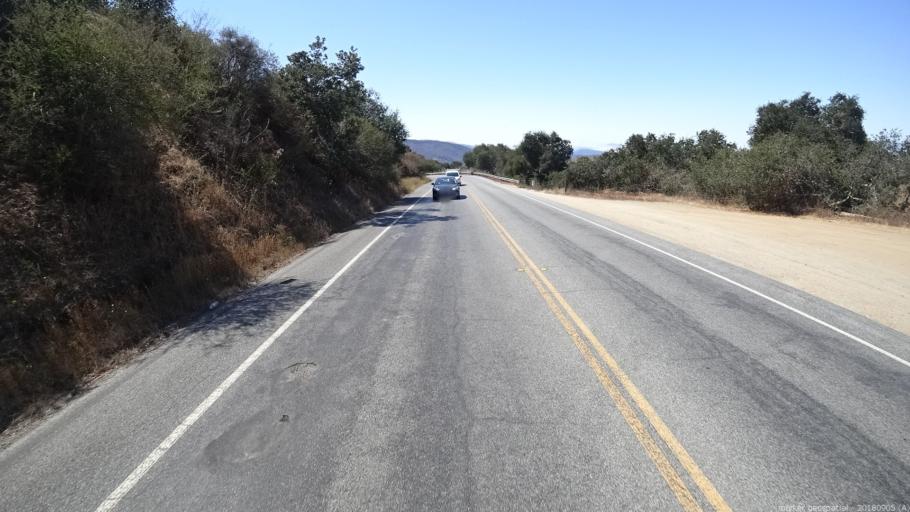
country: US
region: California
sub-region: Monterey County
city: Carmel Valley Village
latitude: 36.5276
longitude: -121.7534
